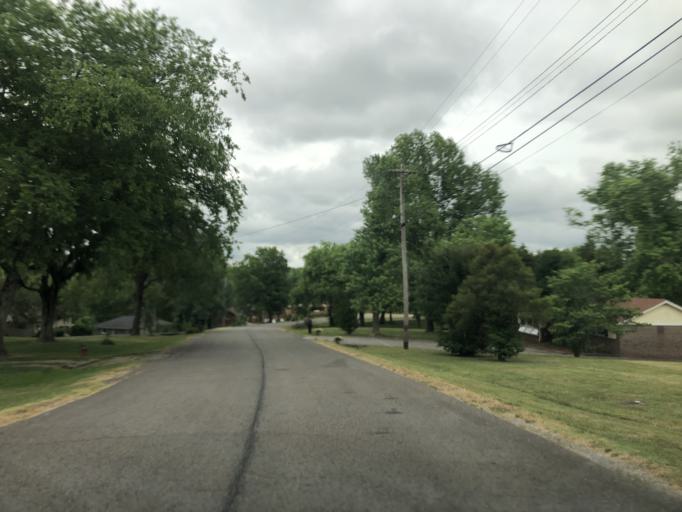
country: US
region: Tennessee
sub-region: Davidson County
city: Goodlettsville
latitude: 36.2637
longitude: -86.7696
